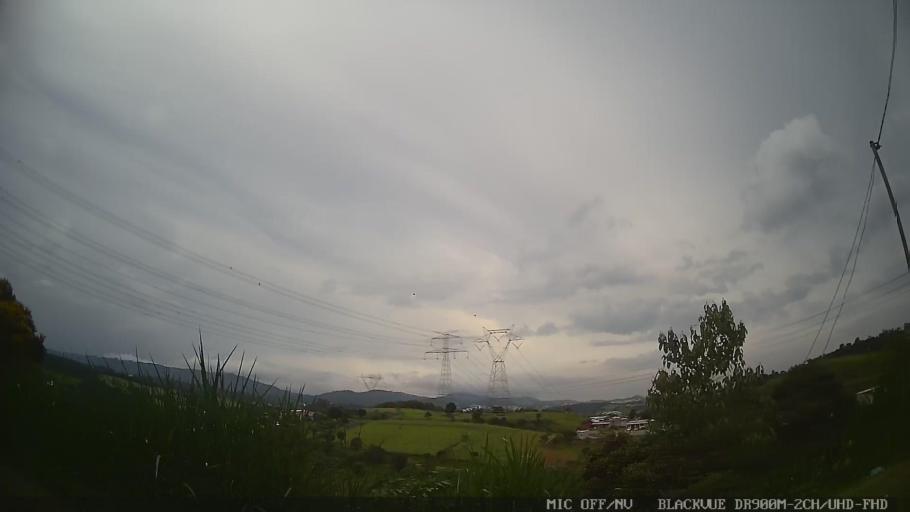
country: BR
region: Sao Paulo
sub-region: Aruja
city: Aruja
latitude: -23.4474
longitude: -46.2825
